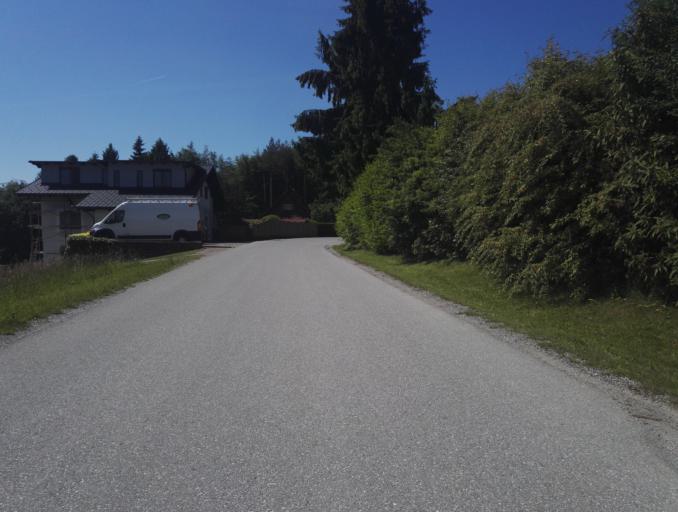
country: AT
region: Styria
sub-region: Politischer Bezirk Graz-Umgebung
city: Edelsgrub
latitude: 47.0525
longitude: 15.5747
